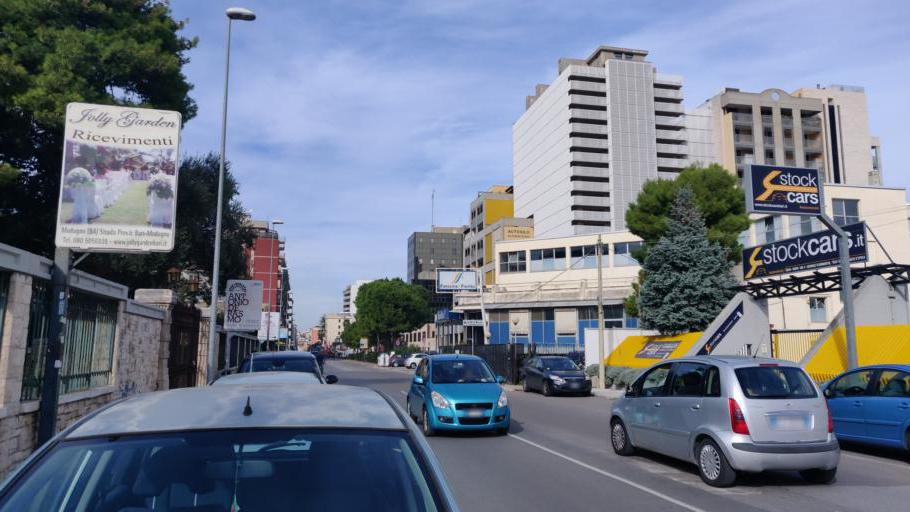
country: IT
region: Apulia
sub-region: Provincia di Bari
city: Bari
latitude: 41.1116
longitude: 16.8826
